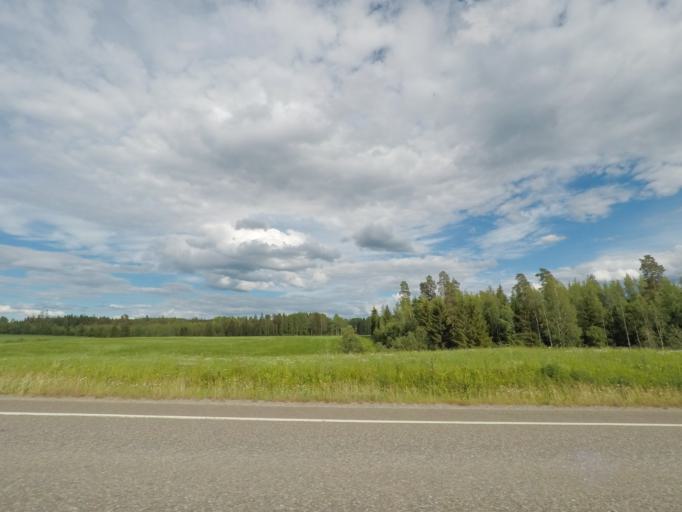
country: FI
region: Paijanne Tavastia
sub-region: Lahti
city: Hollola
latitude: 60.8228
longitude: 25.4871
